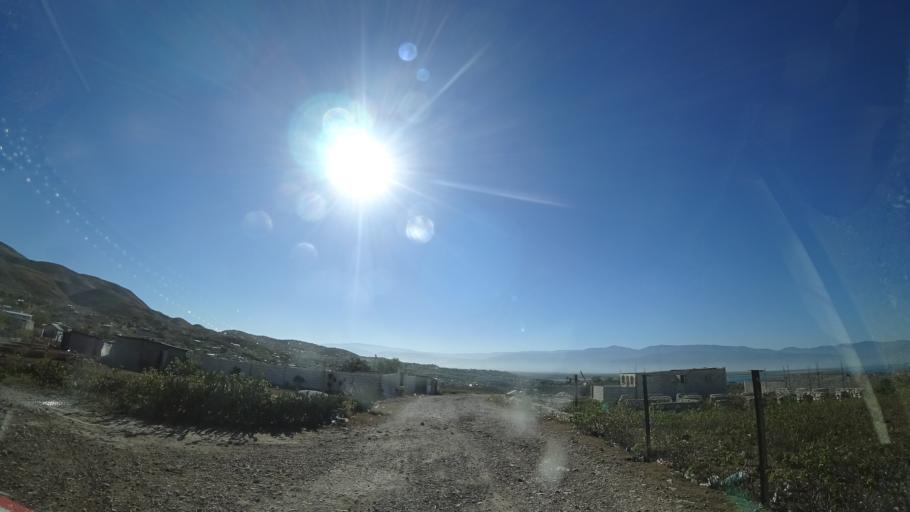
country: HT
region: Ouest
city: Cabaret
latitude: 18.6900
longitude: -72.3181
